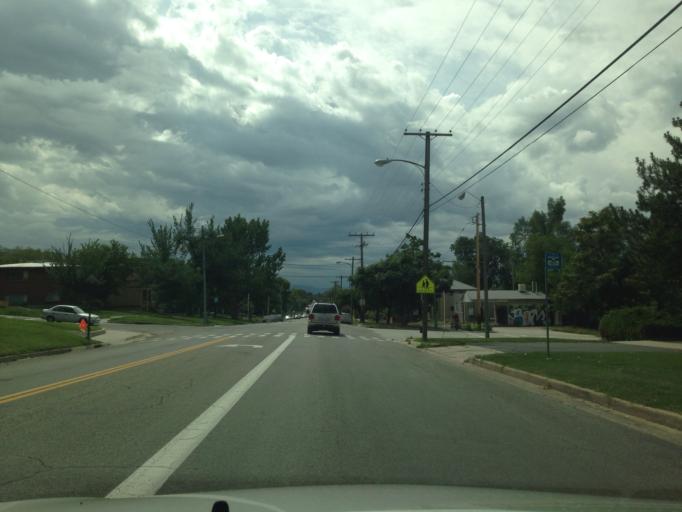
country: US
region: Utah
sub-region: Salt Lake County
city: Salt Lake City
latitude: 40.7591
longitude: -111.8654
